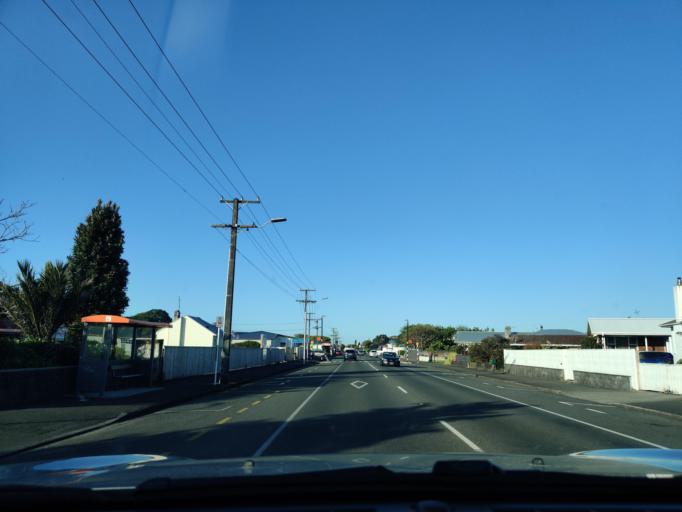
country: NZ
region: Taranaki
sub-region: New Plymouth District
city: New Plymouth
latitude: -39.0746
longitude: 174.0578
